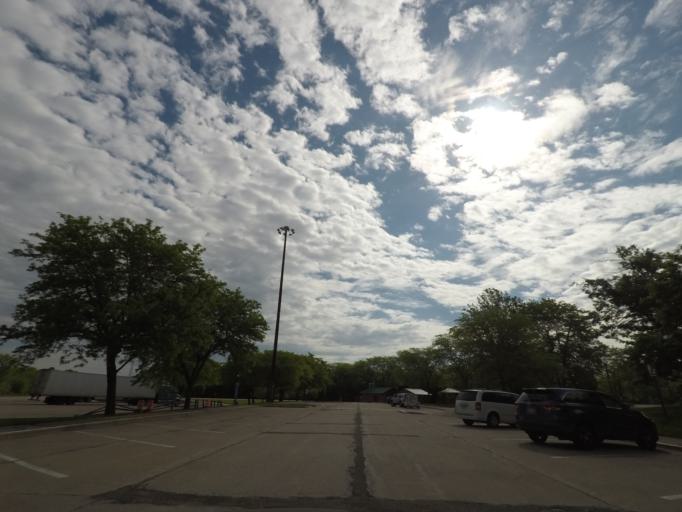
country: US
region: Illinois
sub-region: McLean County
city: Twin Grove
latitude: 40.3598
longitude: -89.1103
